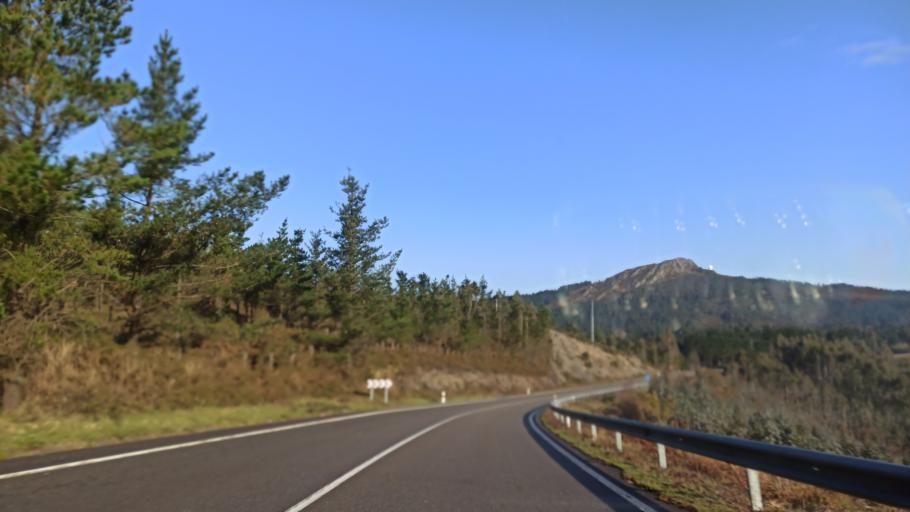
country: ES
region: Galicia
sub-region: Provincia da Coruna
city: As Pontes de Garcia Rodriguez
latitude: 43.4976
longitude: -7.8306
